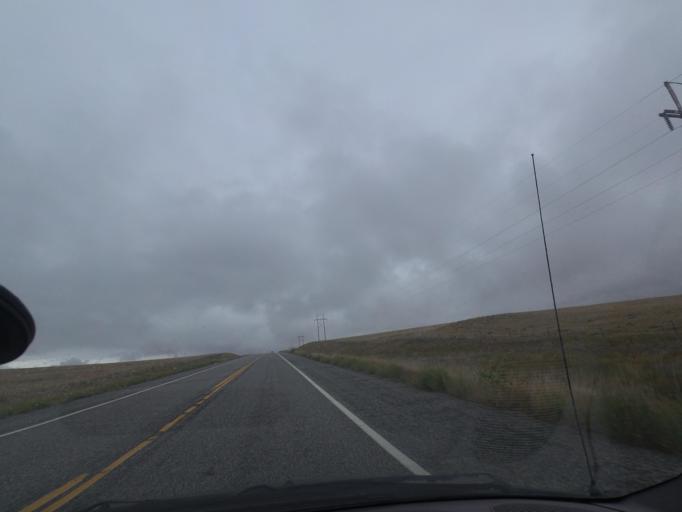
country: US
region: Colorado
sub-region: Lincoln County
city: Limon
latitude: 39.7399
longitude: -103.5365
